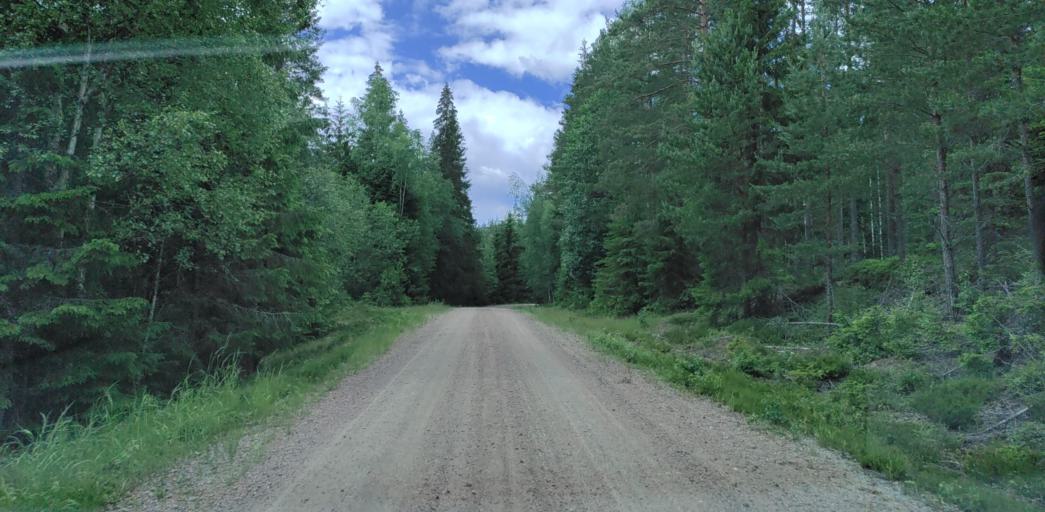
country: SE
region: Vaermland
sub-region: Hagfors Kommun
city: Ekshaerad
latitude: 60.0902
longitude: 13.4138
